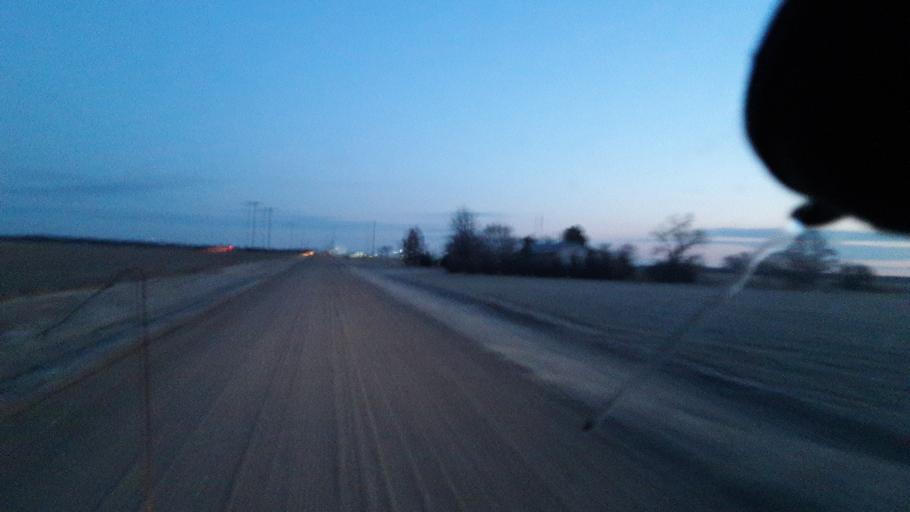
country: US
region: Kansas
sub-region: Reno County
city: South Hutchinson
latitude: 38.0065
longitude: -97.9767
